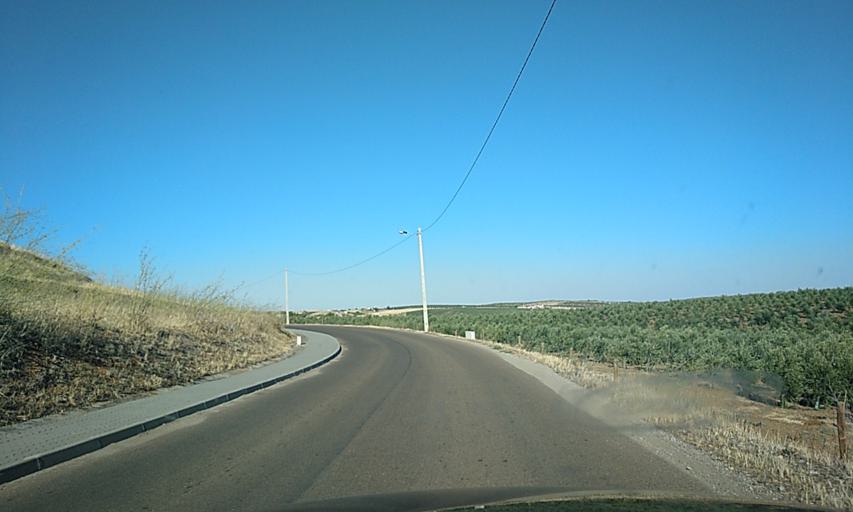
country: PT
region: Portalegre
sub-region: Campo Maior
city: Campo Maior
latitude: 39.0078
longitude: -7.0697
